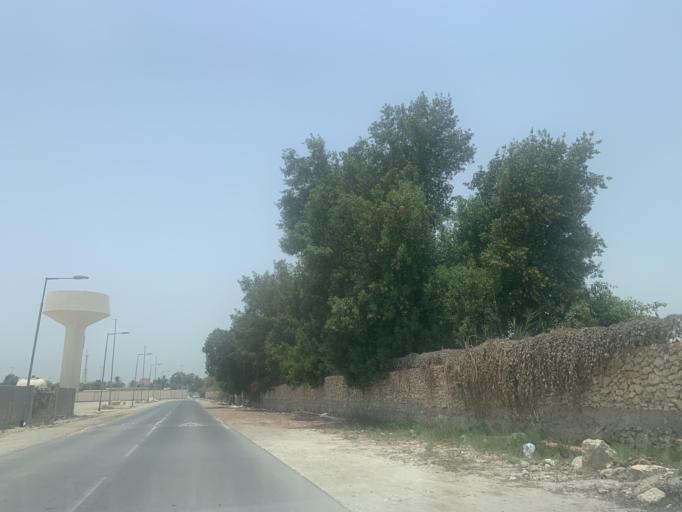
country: BH
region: Manama
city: Jidd Hafs
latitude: 26.2178
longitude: 50.4579
